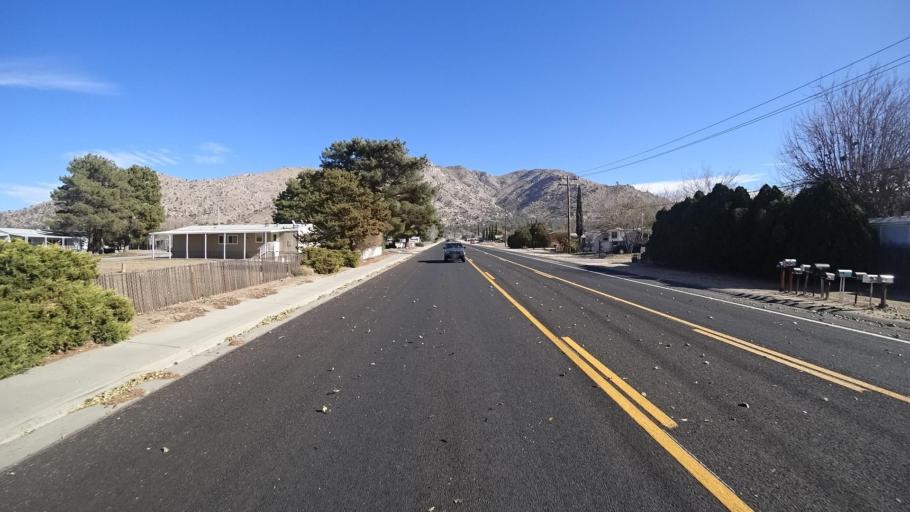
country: US
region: California
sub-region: Kern County
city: Lake Isabella
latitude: 35.6166
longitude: -118.4742
